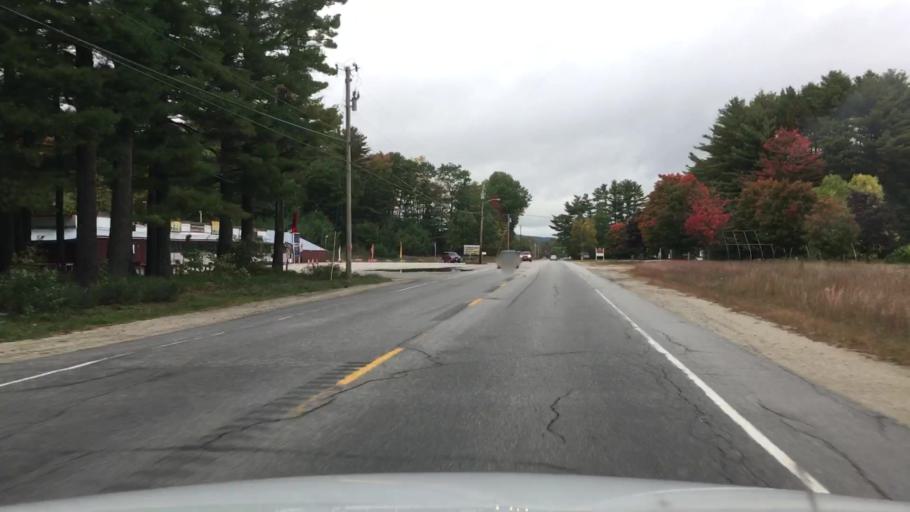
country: US
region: Maine
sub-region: Oxford County
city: Oxford
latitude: 44.1584
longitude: -70.4932
